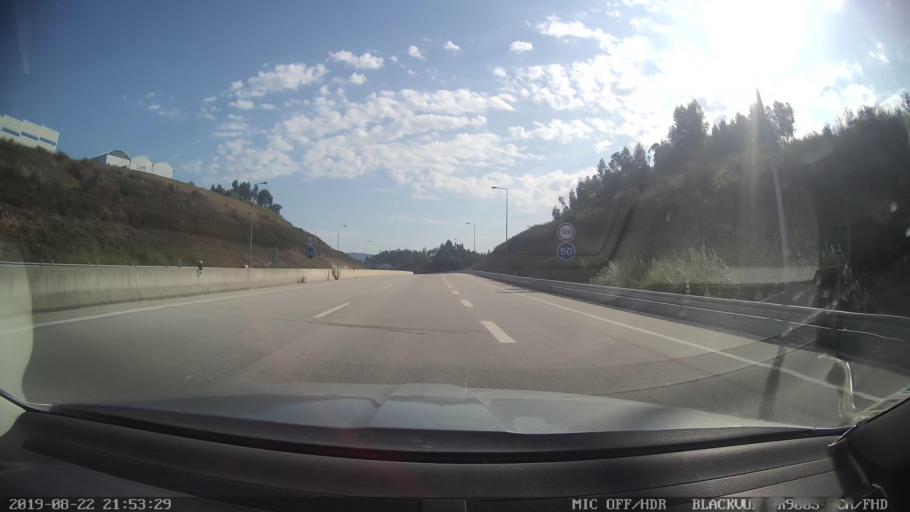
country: PT
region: Coimbra
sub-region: Miranda do Corvo
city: Miranda do Corvo
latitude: 40.1181
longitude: -8.3873
